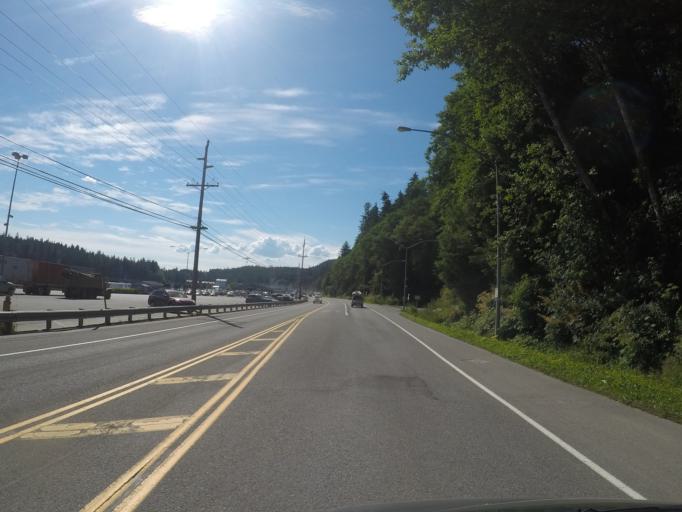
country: US
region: Alaska
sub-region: Juneau City and Borough
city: Juneau
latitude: 58.3825
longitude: -134.6826
